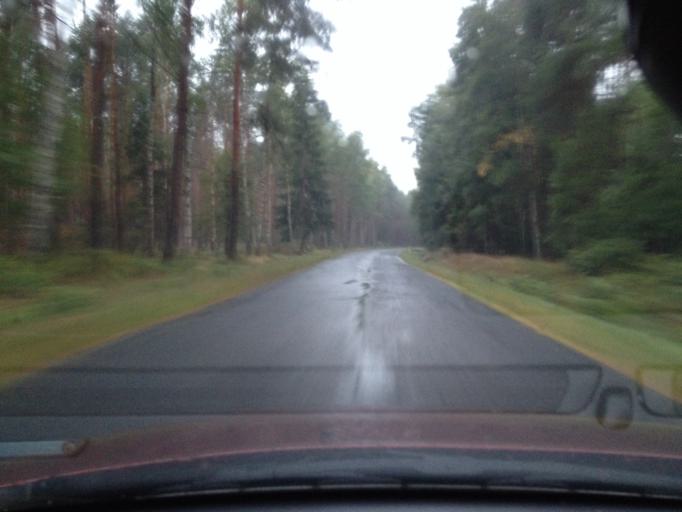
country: PL
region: Lubusz
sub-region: Powiat zaganski
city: Gozdnica
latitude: 51.3448
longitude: 15.1168
